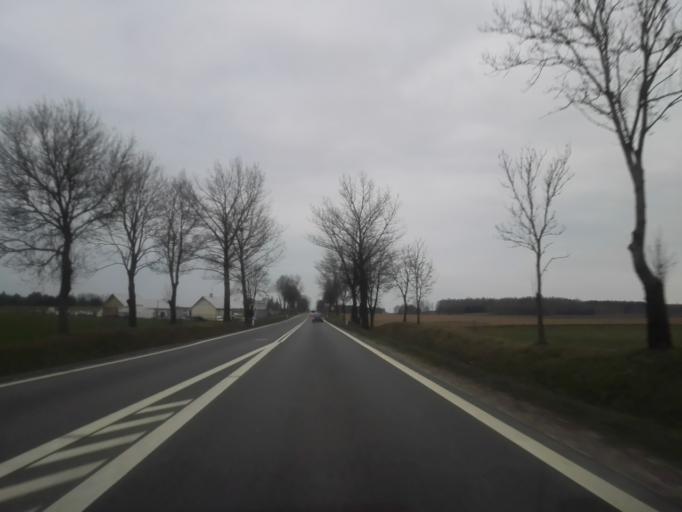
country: PL
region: Podlasie
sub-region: Powiat kolnenski
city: Stawiski
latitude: 53.4594
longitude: 22.1949
